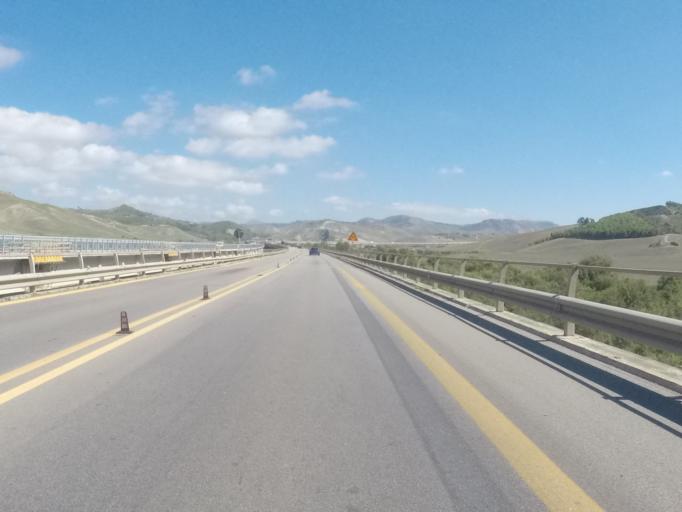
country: IT
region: Sicily
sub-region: Enna
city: Villarosa
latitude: 37.5495
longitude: 14.1825
